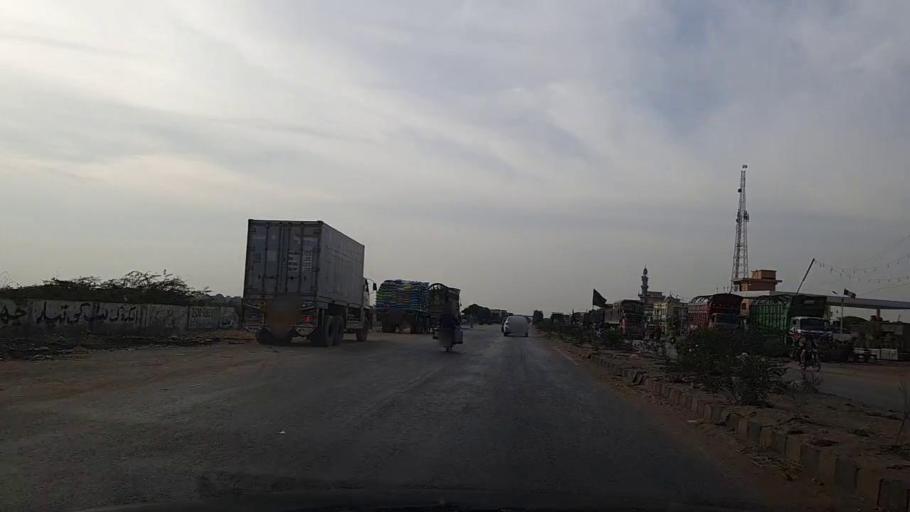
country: PK
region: Sindh
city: Gharo
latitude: 24.8491
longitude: 67.4273
